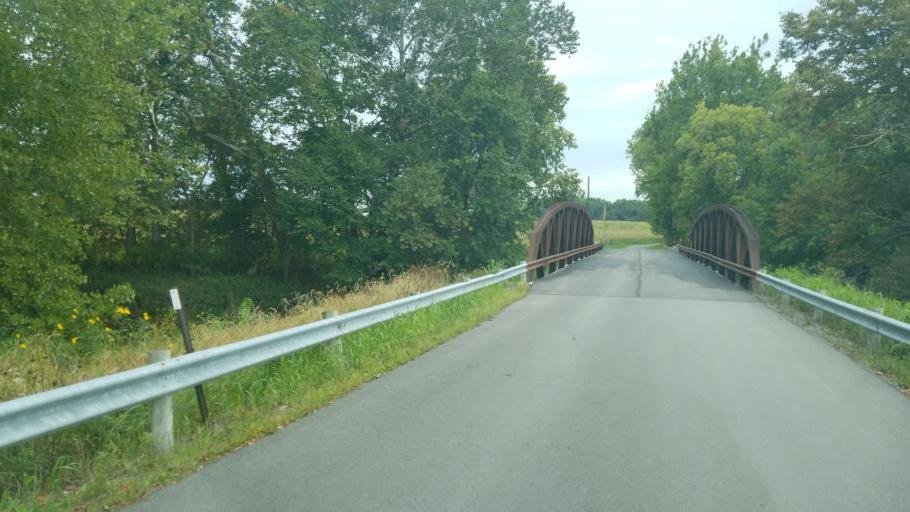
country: US
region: Ohio
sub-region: Wyandot County
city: Upper Sandusky
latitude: 40.7599
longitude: -83.1883
